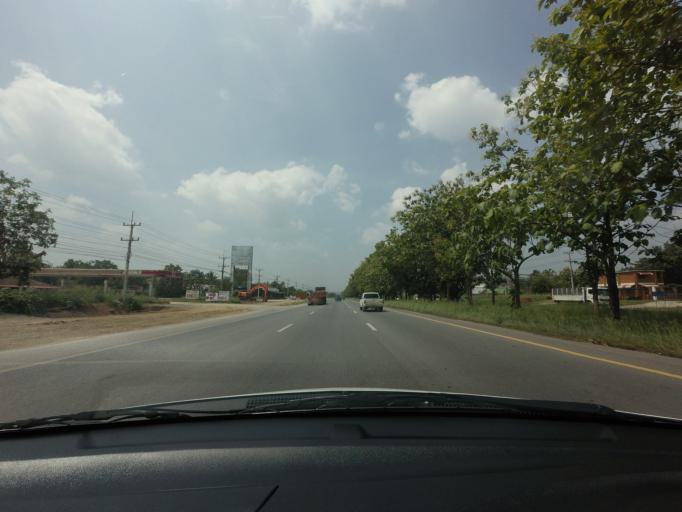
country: TH
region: Nakhon Ratchasima
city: Pak Chong
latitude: 14.6652
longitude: 101.4237
